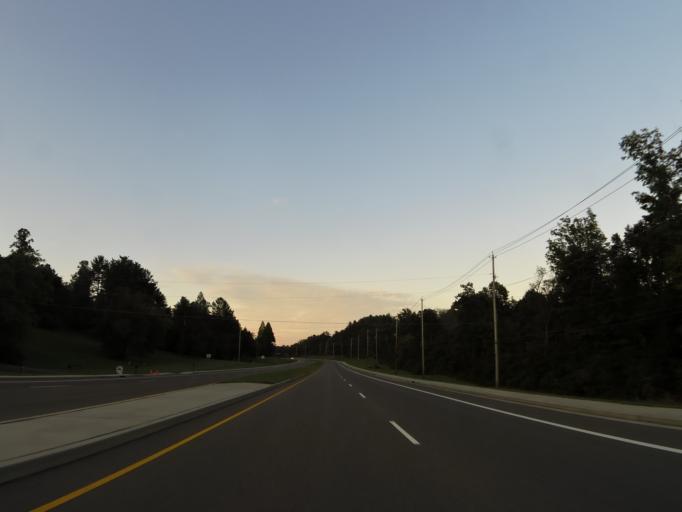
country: US
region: Tennessee
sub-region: Roane County
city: Oliver Springs
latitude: 35.9840
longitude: -84.3286
